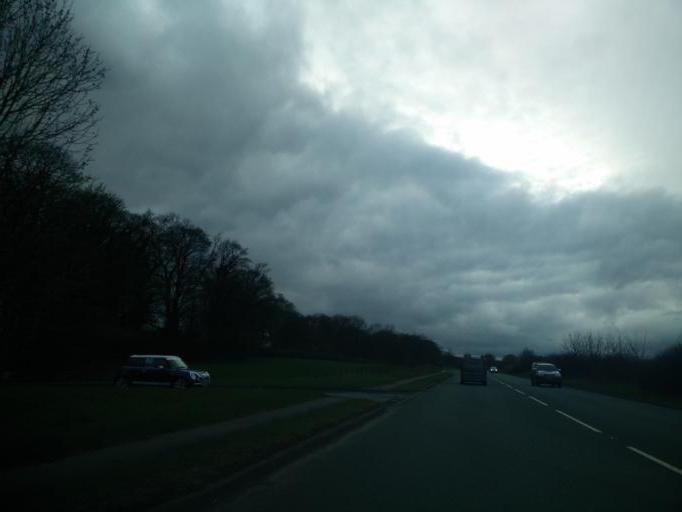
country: GB
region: England
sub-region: County Durham
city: Ushaw Moor
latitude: 54.7414
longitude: -1.6427
